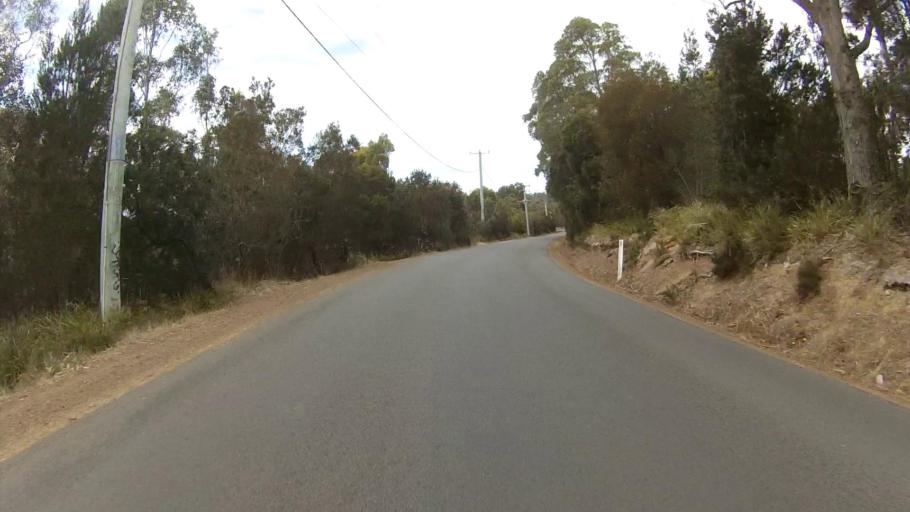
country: AU
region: Tasmania
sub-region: Kingborough
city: Blackmans Bay
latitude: -43.0234
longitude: 147.3002
